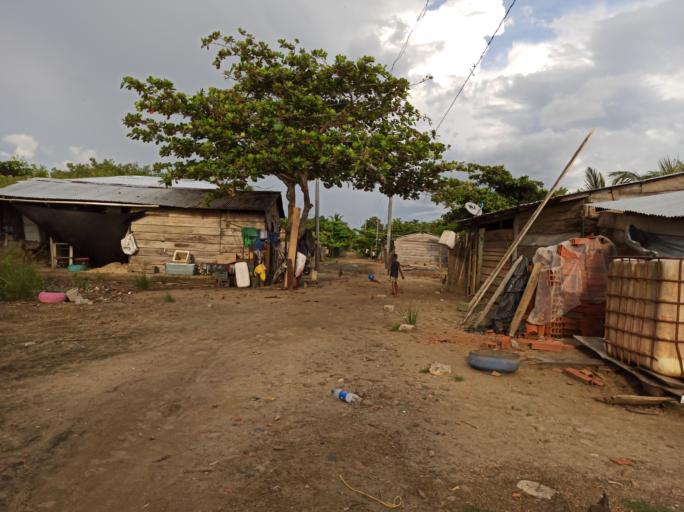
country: CO
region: Antioquia
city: Turbo
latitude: 8.0246
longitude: -76.7307
